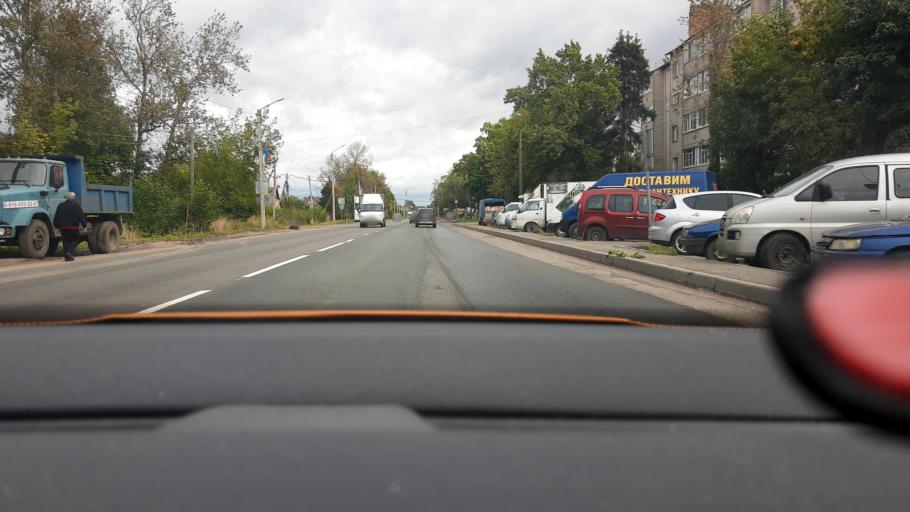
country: RU
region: Moskovskaya
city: Kostino
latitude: 56.0455
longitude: 37.9811
